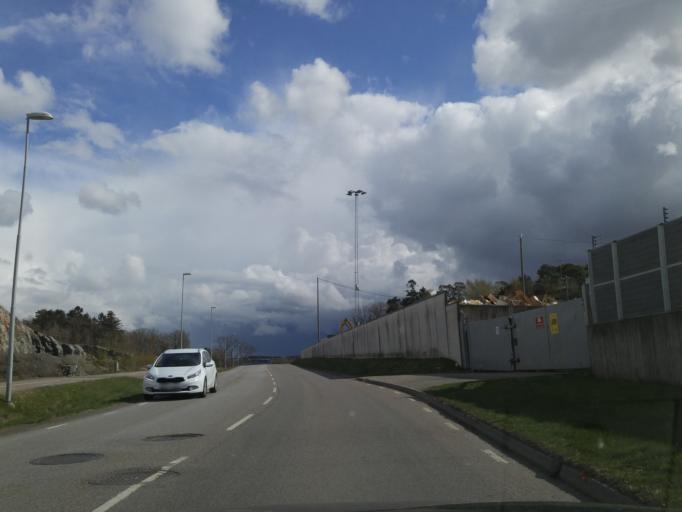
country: SE
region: Vaestra Goetaland
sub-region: Goteborg
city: Majorna
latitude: 57.6570
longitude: 11.9489
